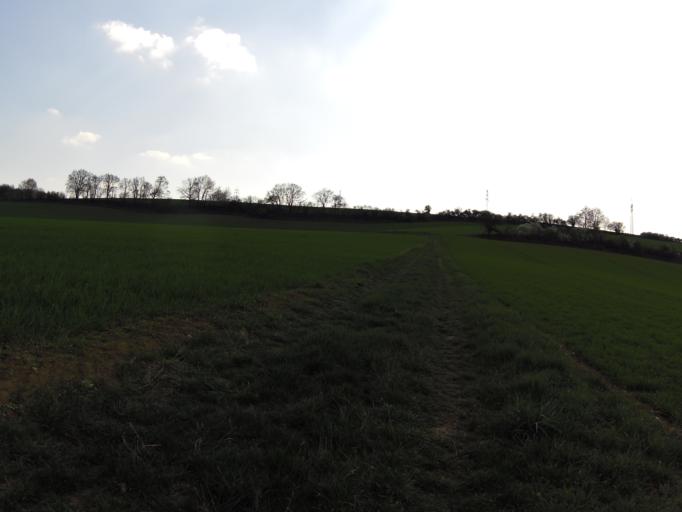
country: DE
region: Bavaria
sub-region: Regierungsbezirk Unterfranken
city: Rottendorf
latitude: 49.7813
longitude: 10.0353
